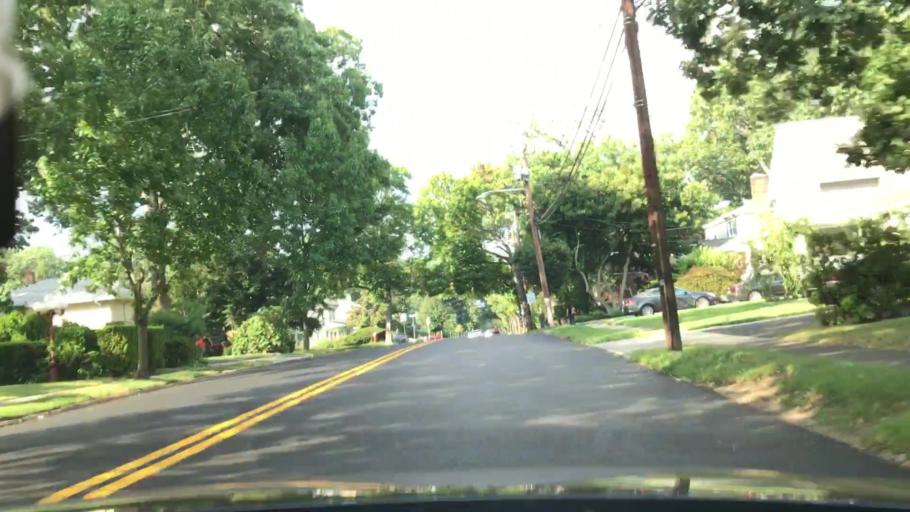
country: US
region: New Jersey
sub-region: Bergen County
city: Maywood
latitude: 40.9060
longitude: -74.0603
